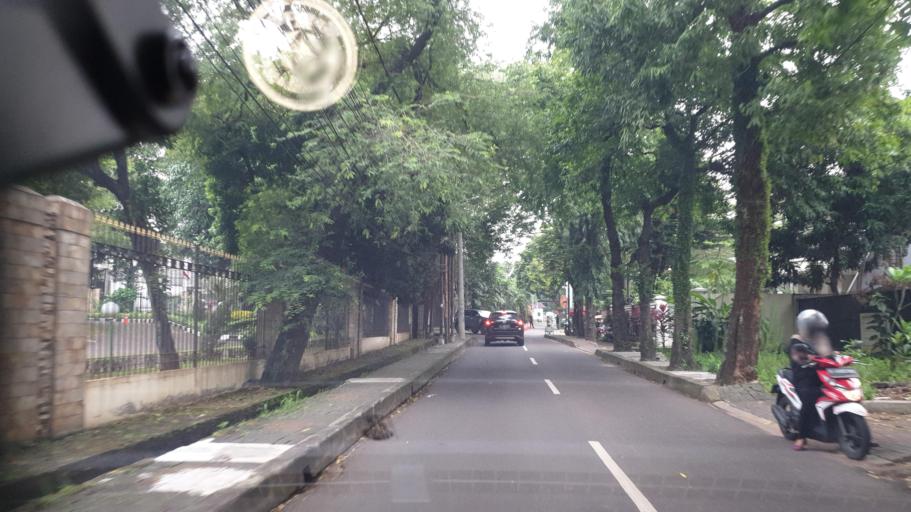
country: ID
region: West Java
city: Pamulang
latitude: -6.3065
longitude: 106.7782
